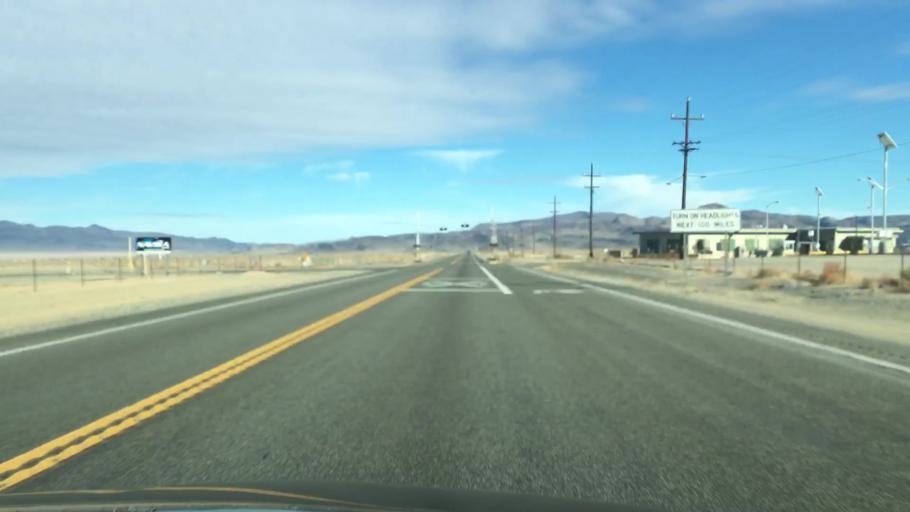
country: US
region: Nevada
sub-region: Mineral County
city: Hawthorne
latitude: 38.5245
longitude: -118.5996
